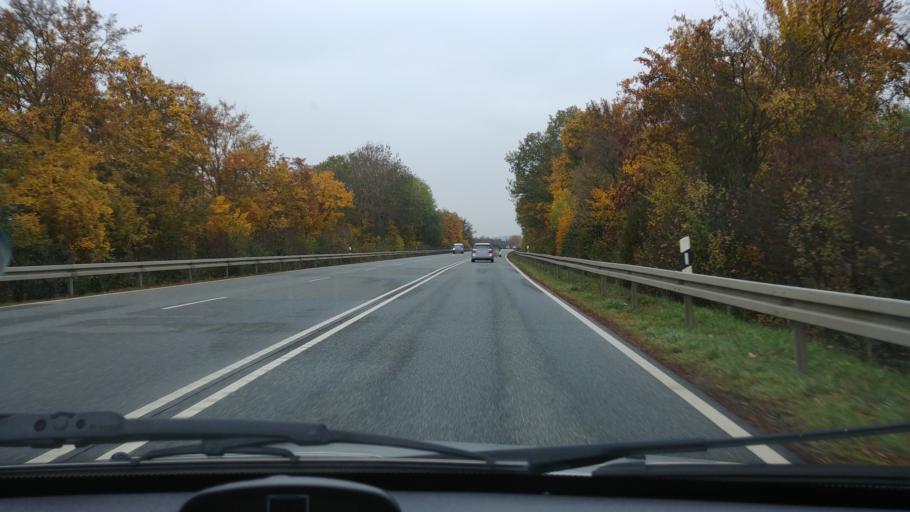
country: DE
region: Hesse
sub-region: Regierungsbezirk Giessen
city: Dehrn
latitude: 50.4472
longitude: 8.0898
